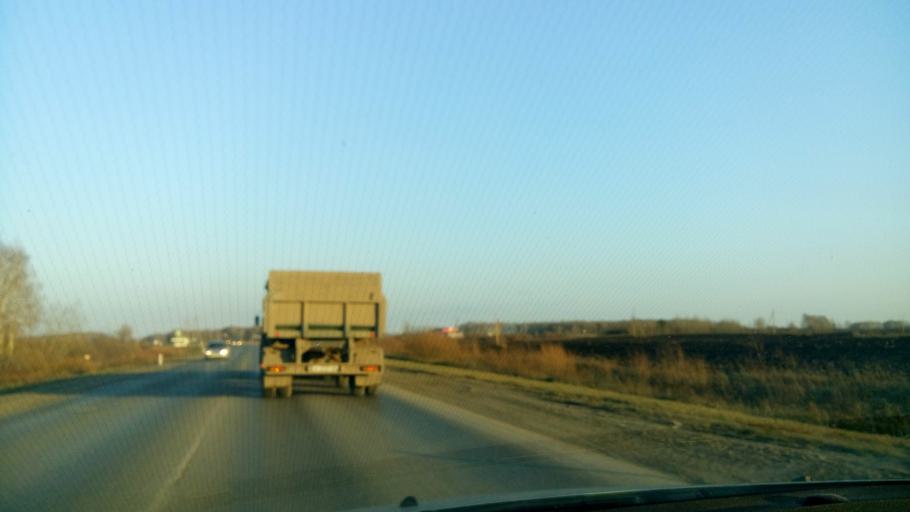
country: RU
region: Sverdlovsk
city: Bogdanovich
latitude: 56.7541
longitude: 62.1005
